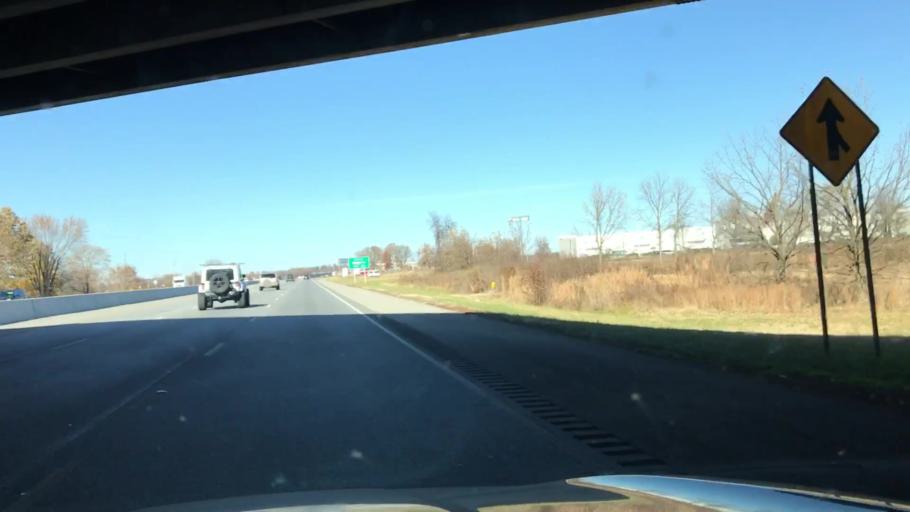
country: US
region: Arkansas
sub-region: Benton County
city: Lowell
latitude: 36.2836
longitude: -94.1565
